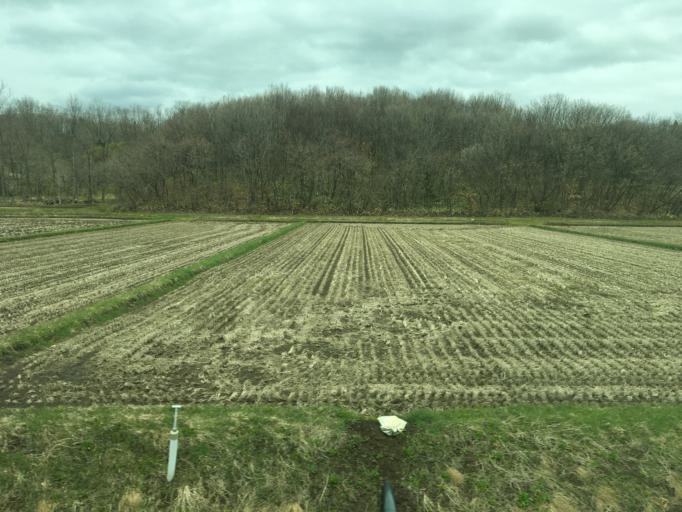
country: JP
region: Aomori
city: Shimokizukuri
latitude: 40.7814
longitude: 140.2715
